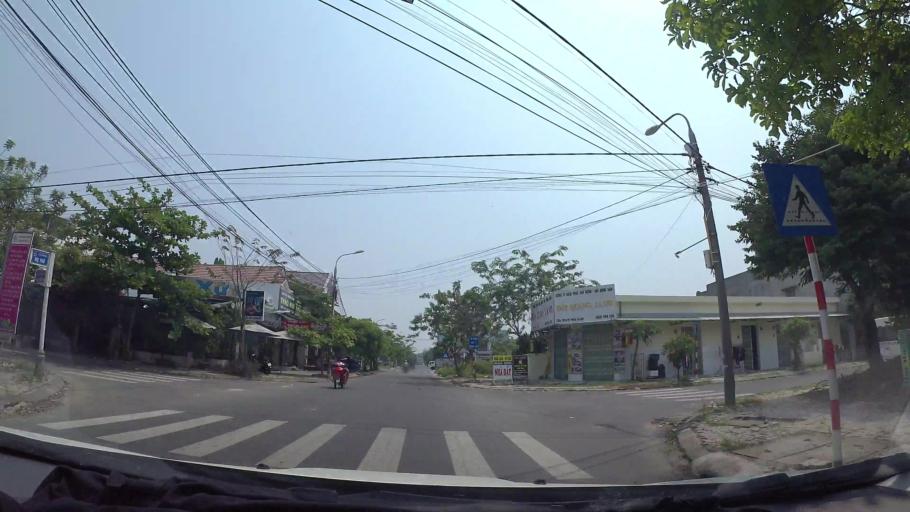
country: VN
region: Da Nang
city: Cam Le
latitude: 16.0000
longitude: 108.2154
